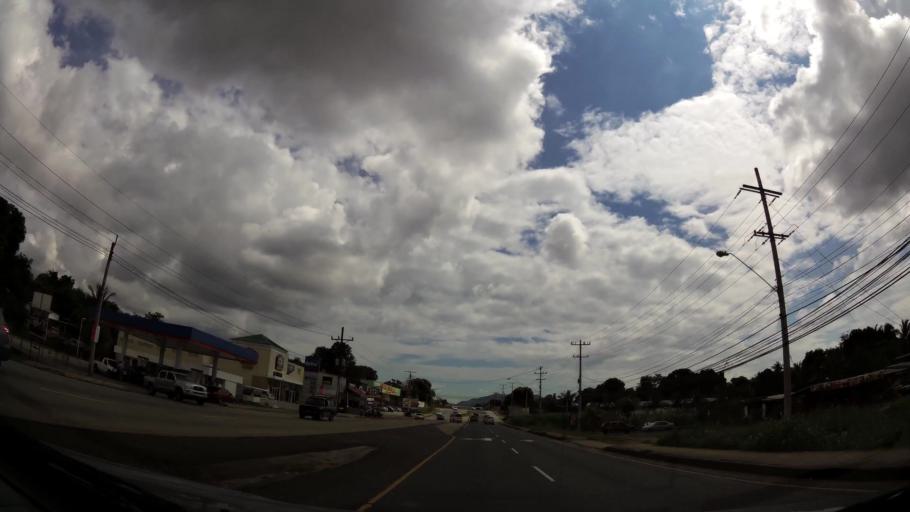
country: PA
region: Panama
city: Nuevo Arraijan
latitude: 8.9269
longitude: -79.7247
